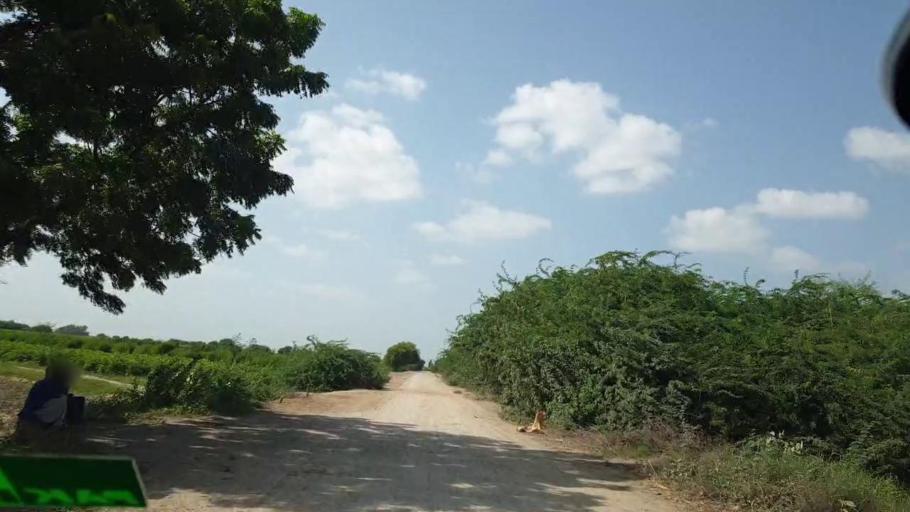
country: PK
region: Sindh
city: Naukot
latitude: 24.6486
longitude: 69.2209
